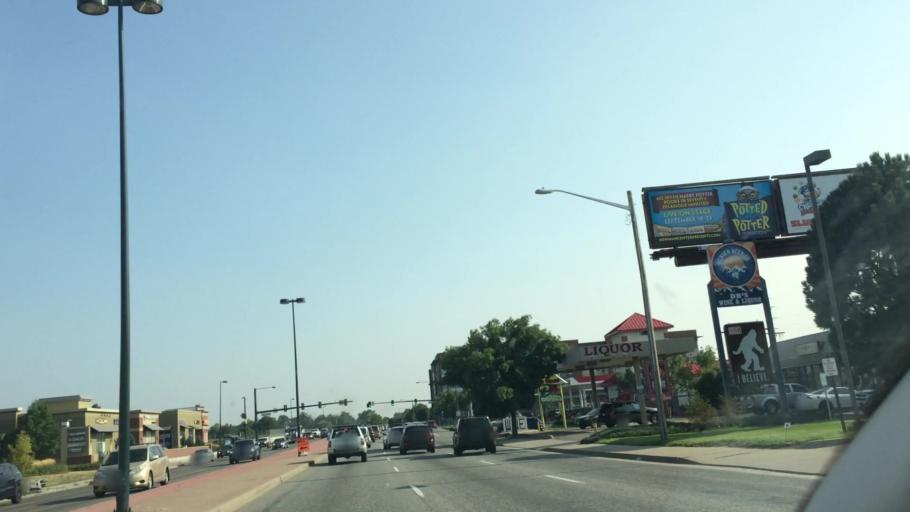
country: US
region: Colorado
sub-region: Adams County
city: Commerce City
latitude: 39.7746
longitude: -104.9406
